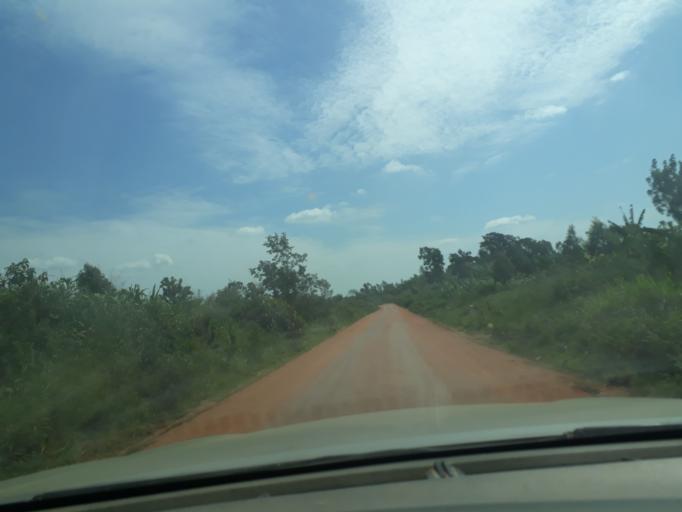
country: UG
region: Northern Region
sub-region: Zombo District
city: Paidha
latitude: 2.1390
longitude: 30.6352
